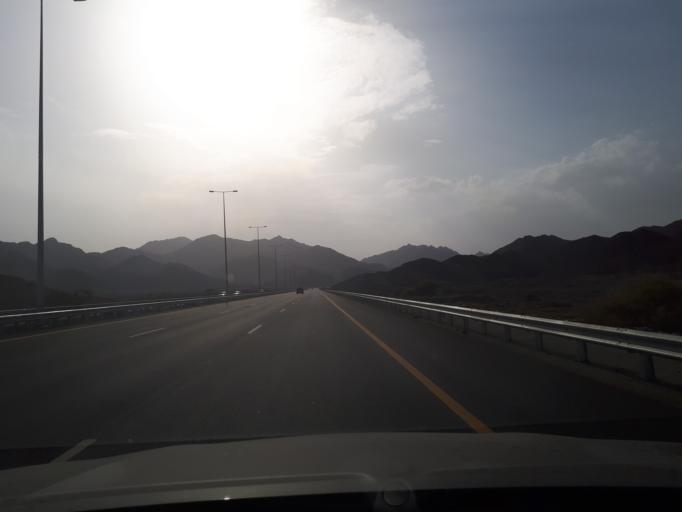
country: OM
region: Ash Sharqiyah
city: Ibra'
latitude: 22.8476
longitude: 58.3295
